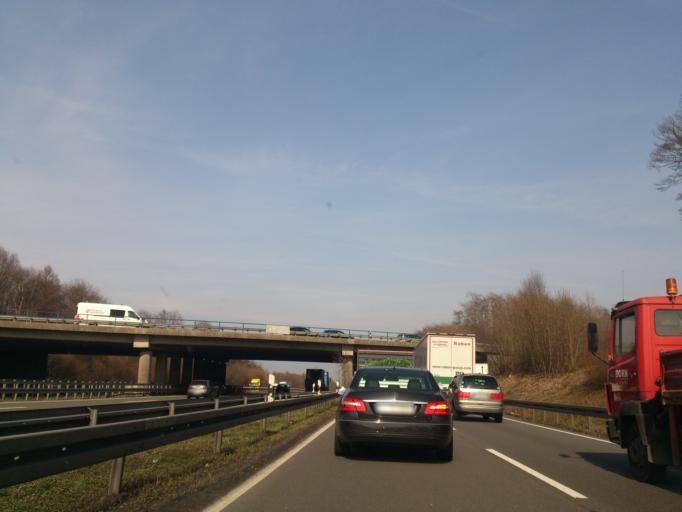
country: DE
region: North Rhine-Westphalia
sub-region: Regierungsbezirk Arnsberg
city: Schwelm
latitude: 51.3128
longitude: 7.2716
